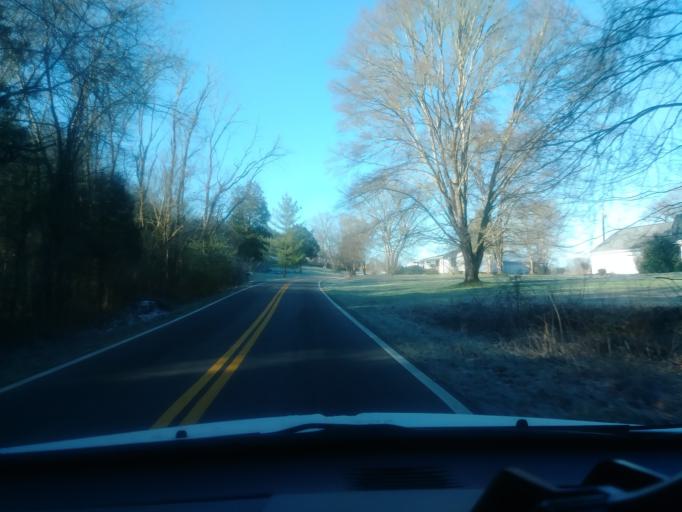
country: US
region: Tennessee
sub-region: Greene County
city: Mosheim
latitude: 36.1216
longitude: -83.0143
